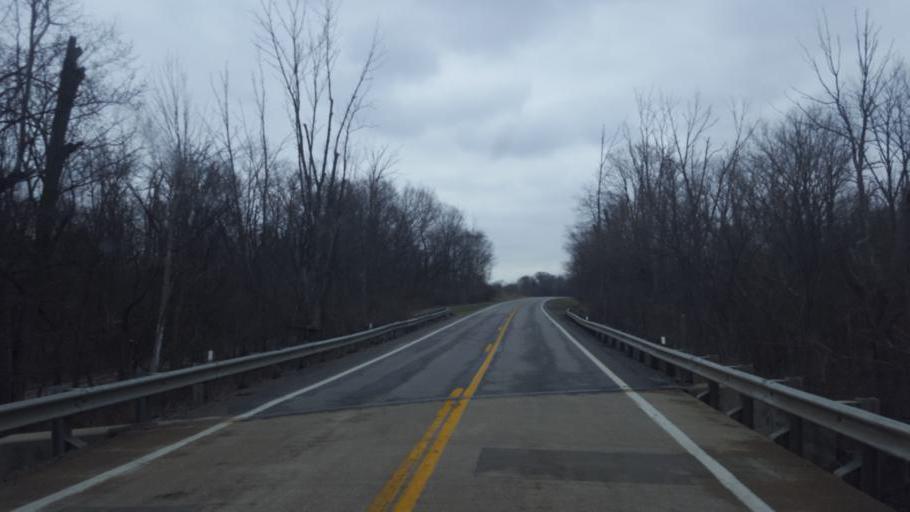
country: US
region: Ohio
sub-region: Delaware County
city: Ashley
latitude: 40.4349
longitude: -83.0590
